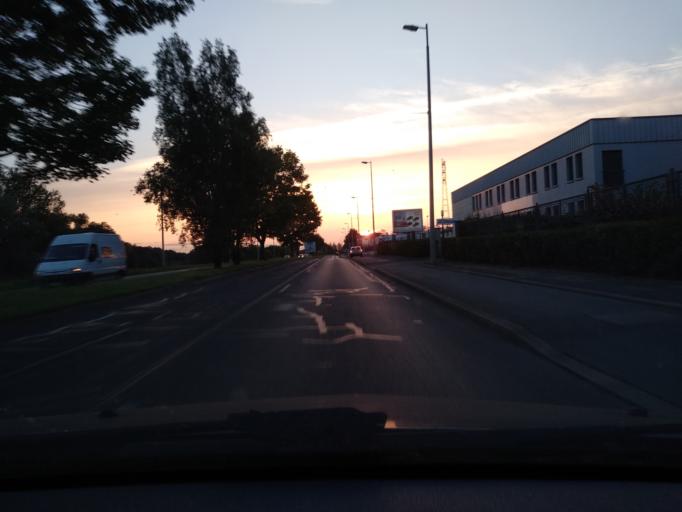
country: FR
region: Centre
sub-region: Departement d'Indre-et-Loire
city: Tours
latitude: 47.3742
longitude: 0.6751
